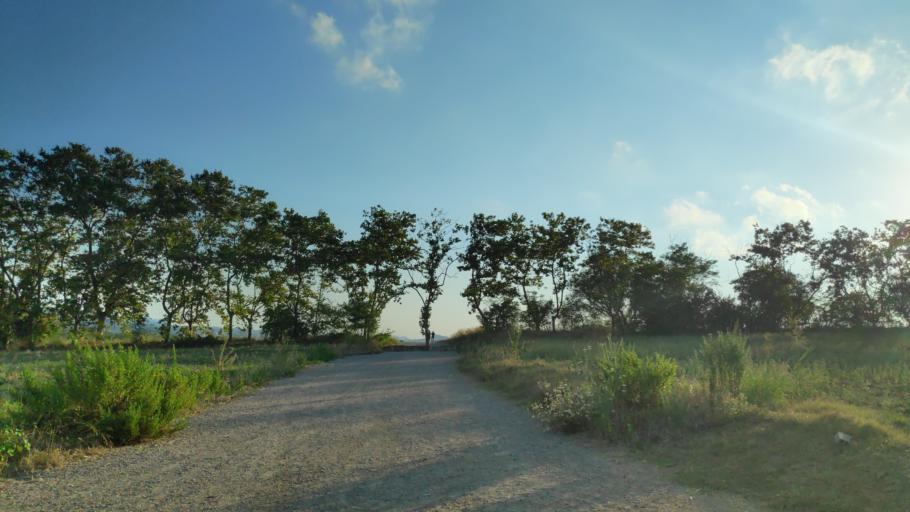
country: ES
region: Catalonia
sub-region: Provincia de Barcelona
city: Cerdanyola del Valles
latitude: 41.4895
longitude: 2.1166
